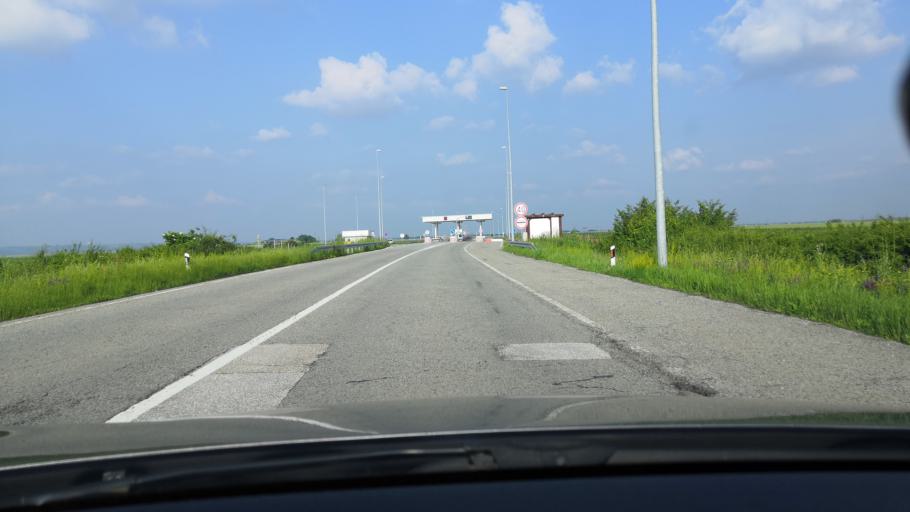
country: RS
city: Beska
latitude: 45.0994
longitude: 20.1007
